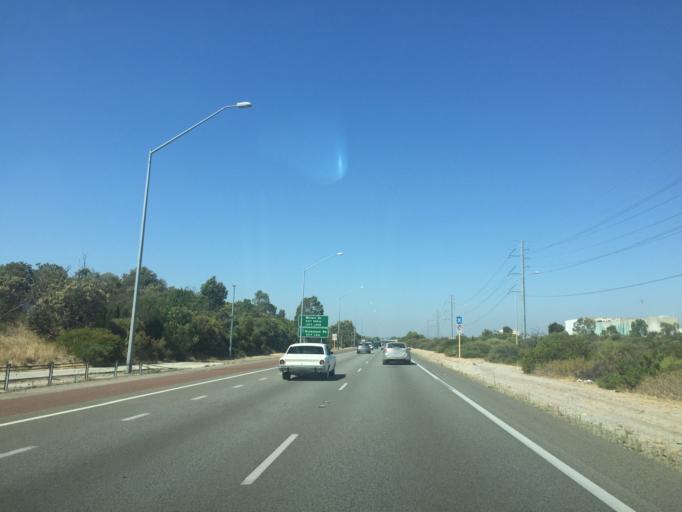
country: AU
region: Western Australia
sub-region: Canning
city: Willetton
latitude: -32.0637
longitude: 115.8964
